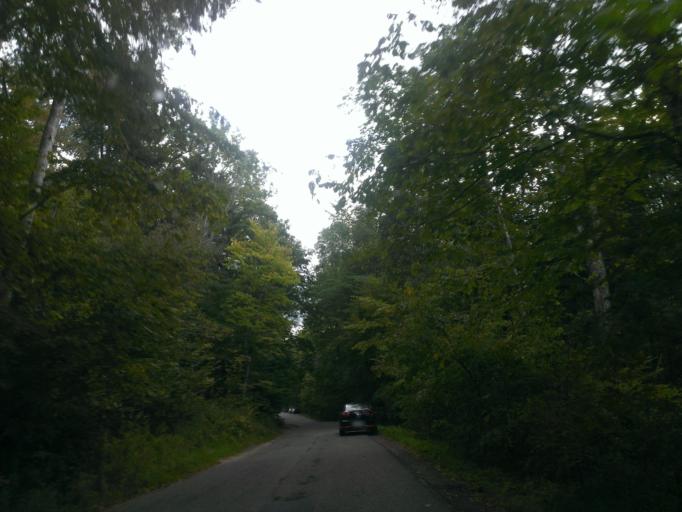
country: LV
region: Sigulda
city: Sigulda
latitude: 57.1627
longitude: 24.8395
